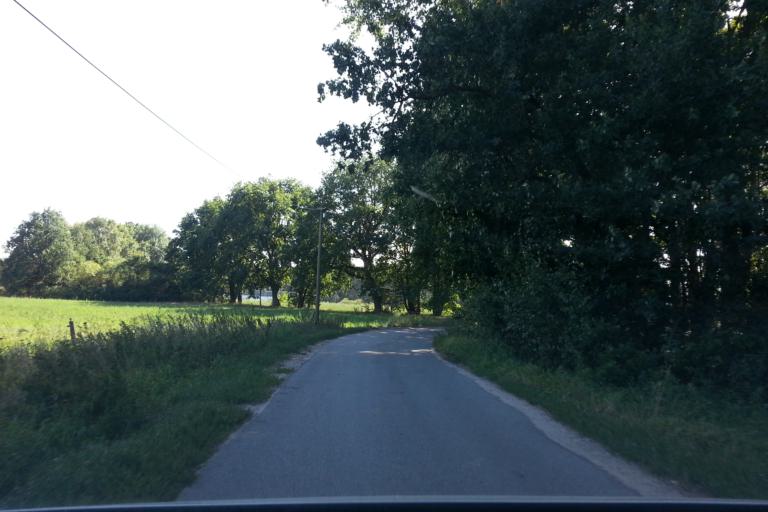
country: DE
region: Mecklenburg-Vorpommern
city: Eggesin
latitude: 53.6929
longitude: 14.0587
